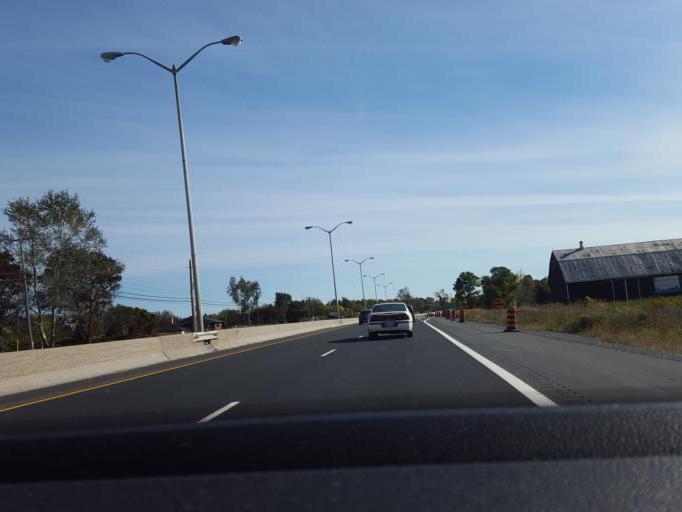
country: CA
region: Ontario
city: Oshawa
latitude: 43.9544
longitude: -78.6075
